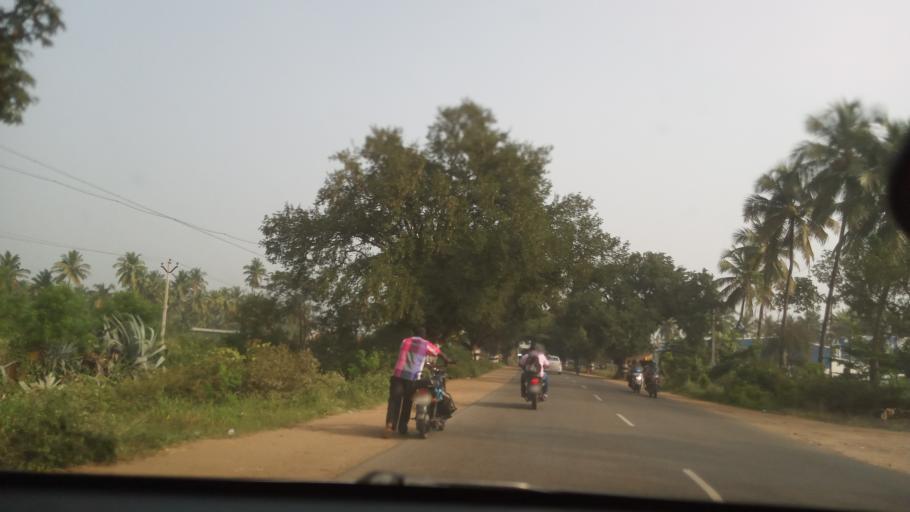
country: IN
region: Tamil Nadu
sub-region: Coimbatore
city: Annur
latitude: 11.1665
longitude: 77.0528
